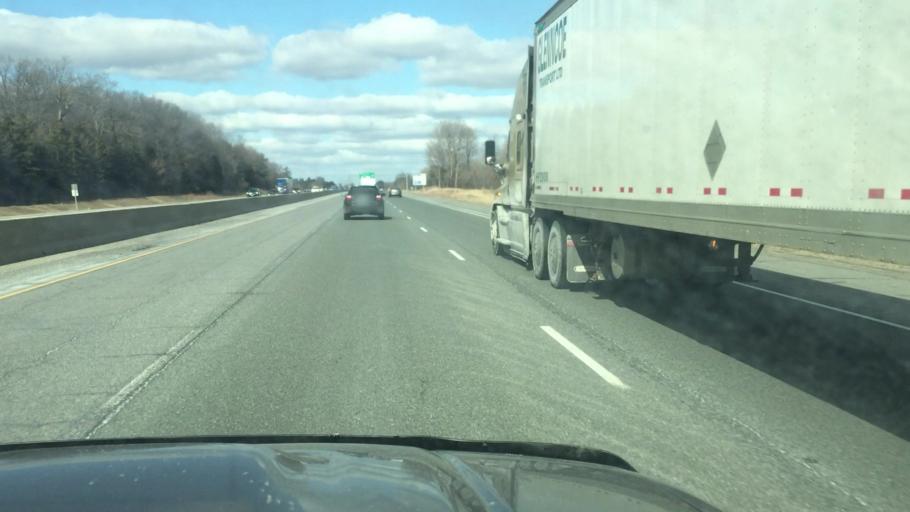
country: CA
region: Ontario
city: Ingersoll
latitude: 43.0163
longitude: -80.8711
